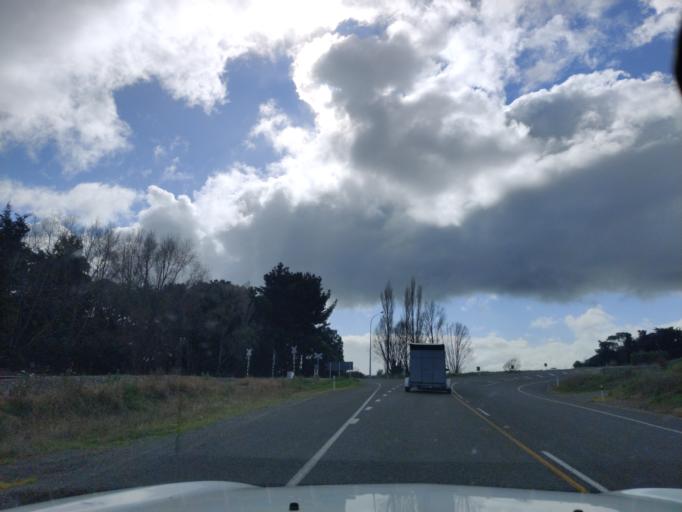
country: NZ
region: Manawatu-Wanganui
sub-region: Palmerston North City
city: Palmerston North
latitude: -40.4556
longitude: 175.5186
